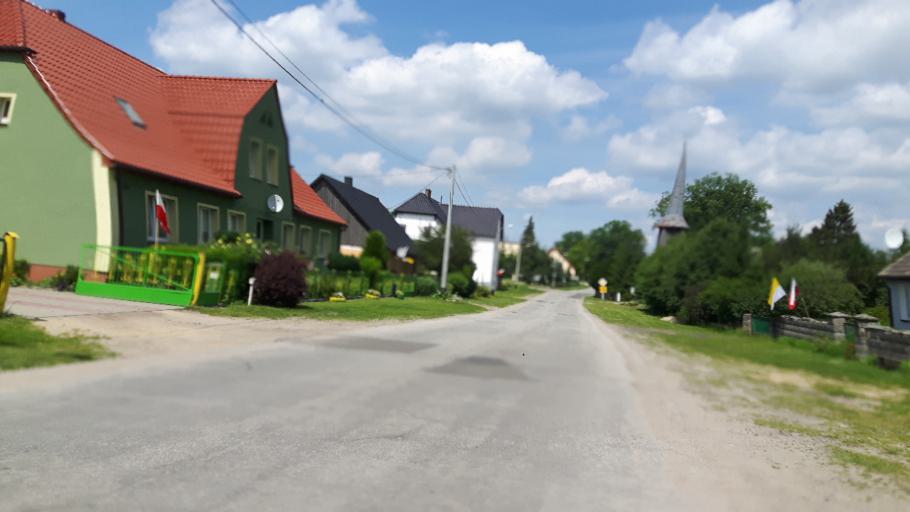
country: PL
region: West Pomeranian Voivodeship
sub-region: Powiat goleniowski
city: Osina
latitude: 53.6592
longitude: 14.9767
